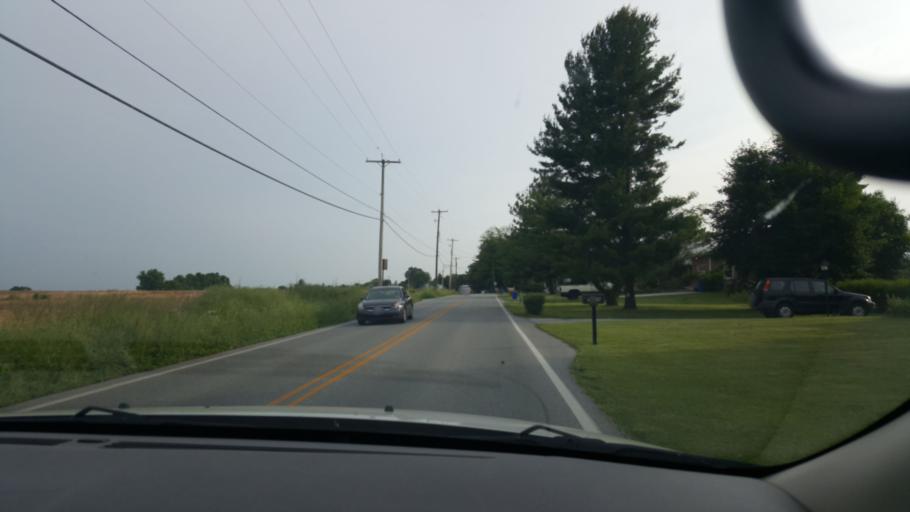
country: US
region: Pennsylvania
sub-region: York County
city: Weigelstown
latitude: 40.0006
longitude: -76.8089
